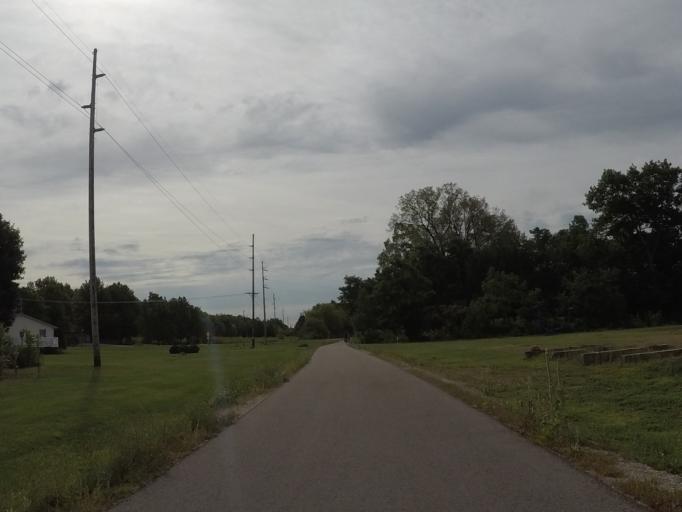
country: US
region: Wisconsin
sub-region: Sauk County
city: Prairie du Sac
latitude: 43.3153
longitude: -89.7364
